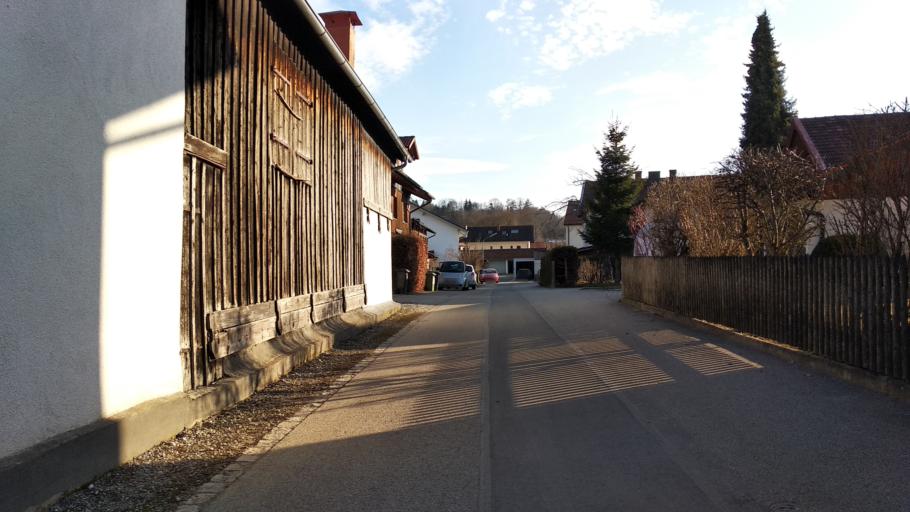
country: DE
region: Bavaria
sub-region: Upper Bavaria
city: Glonn
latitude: 47.9842
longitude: 11.8649
